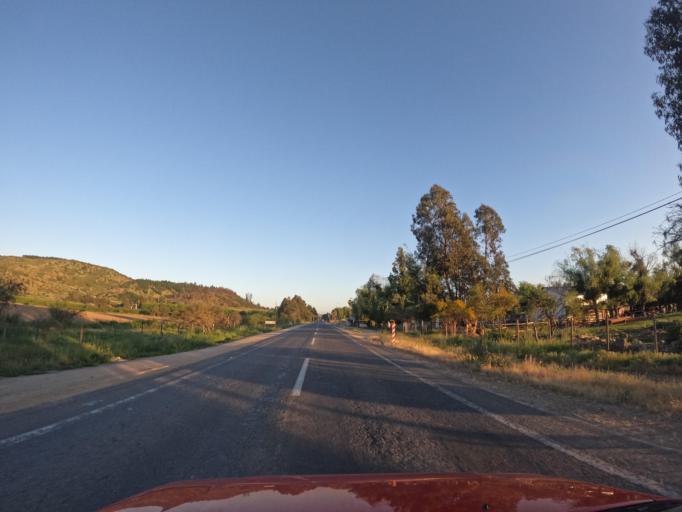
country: CL
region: Maule
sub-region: Provincia de Talca
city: Talca
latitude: -35.0834
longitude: -71.6710
